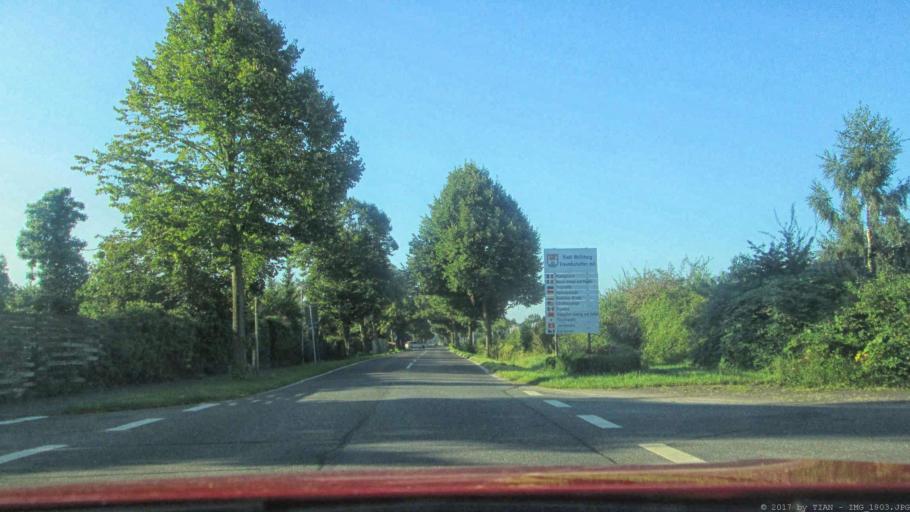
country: DE
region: Lower Saxony
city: Tiddische
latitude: 52.4755
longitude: 10.8209
